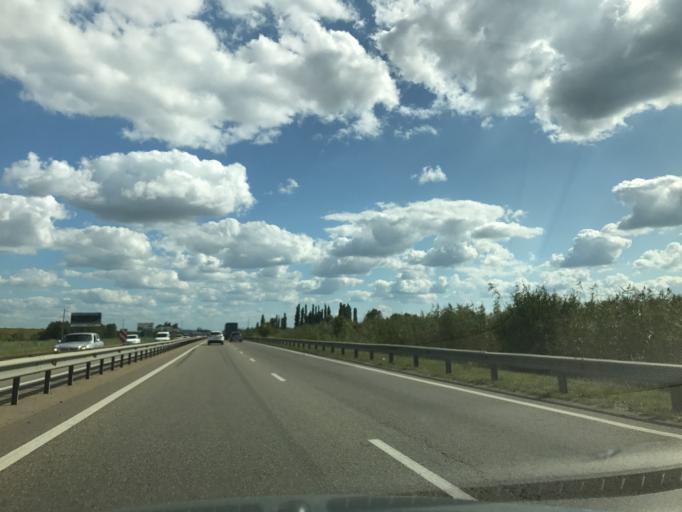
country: RU
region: Adygeya
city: Tlyustenkhabl'
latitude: 44.9322
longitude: 39.1365
